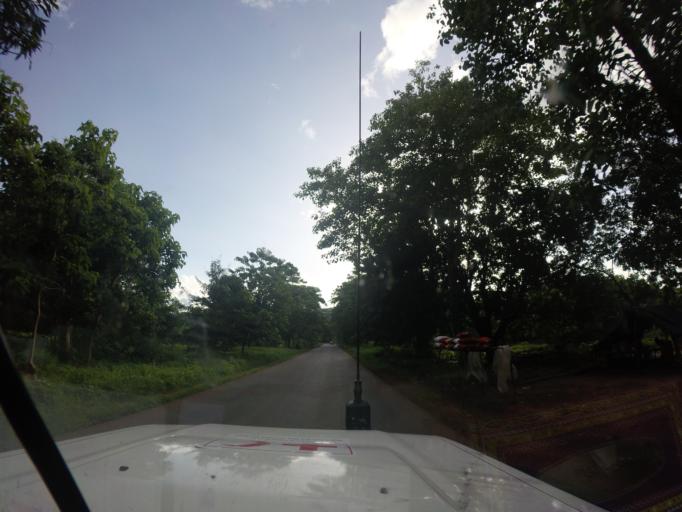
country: GN
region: Kindia
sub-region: Kindia
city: Kindia
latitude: 10.0018
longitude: -12.7833
